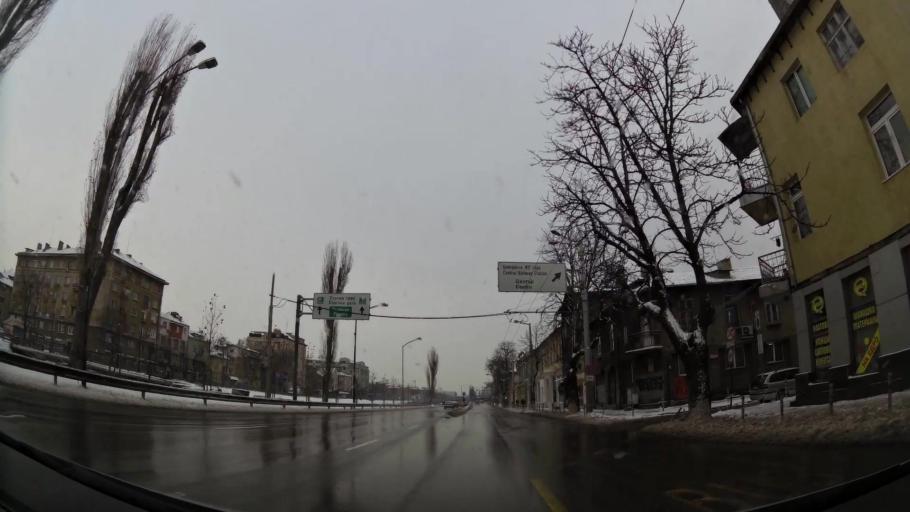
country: BG
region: Sofia-Capital
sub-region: Stolichna Obshtina
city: Sofia
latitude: 42.7050
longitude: 23.3199
